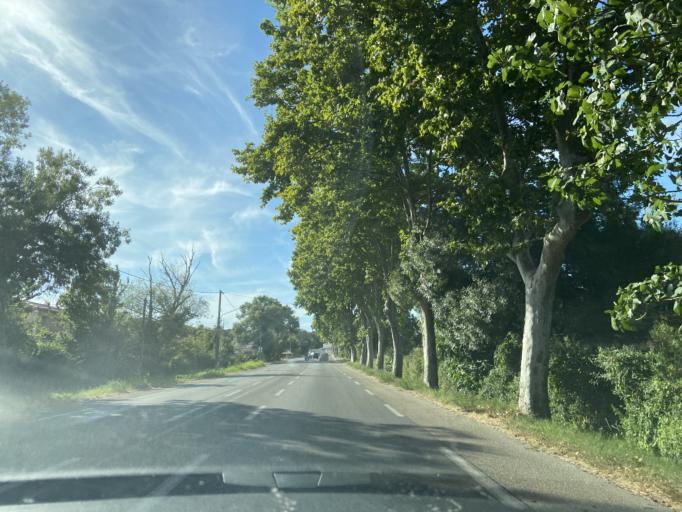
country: FR
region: Provence-Alpes-Cote d'Azur
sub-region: Departement des Bouches-du-Rhone
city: Miramas
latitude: 43.5746
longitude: 5.0171
